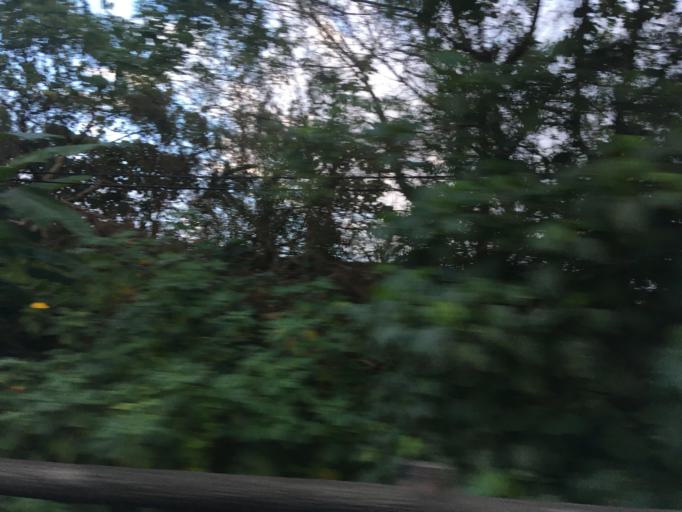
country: TW
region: Taiwan
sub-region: Yilan
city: Yilan
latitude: 24.7553
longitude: 121.7323
